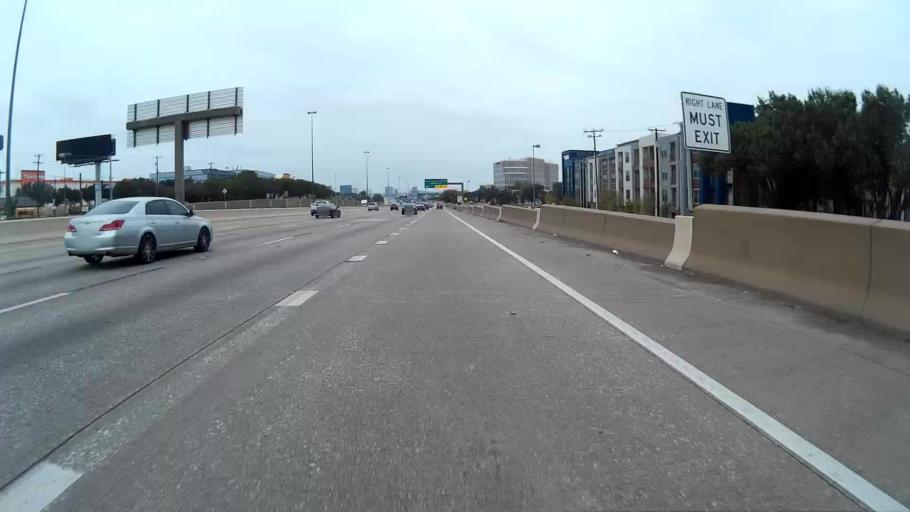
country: US
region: Texas
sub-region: Dallas County
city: University Park
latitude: 32.8891
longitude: -96.7695
